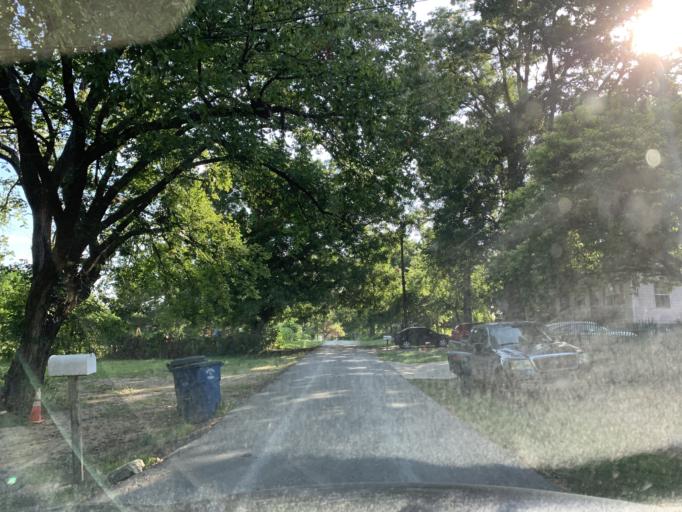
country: US
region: Texas
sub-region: Dallas County
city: Hutchins
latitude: 32.6783
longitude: -96.7781
